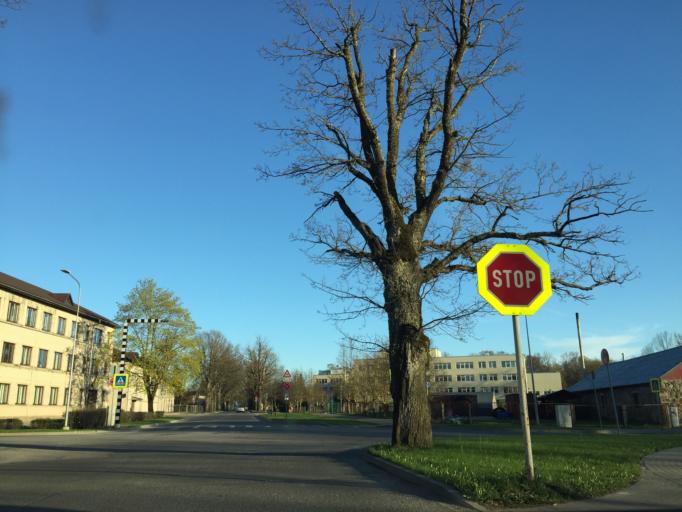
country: LV
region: Valmieras Rajons
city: Valmiera
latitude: 57.5479
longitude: 25.4220
